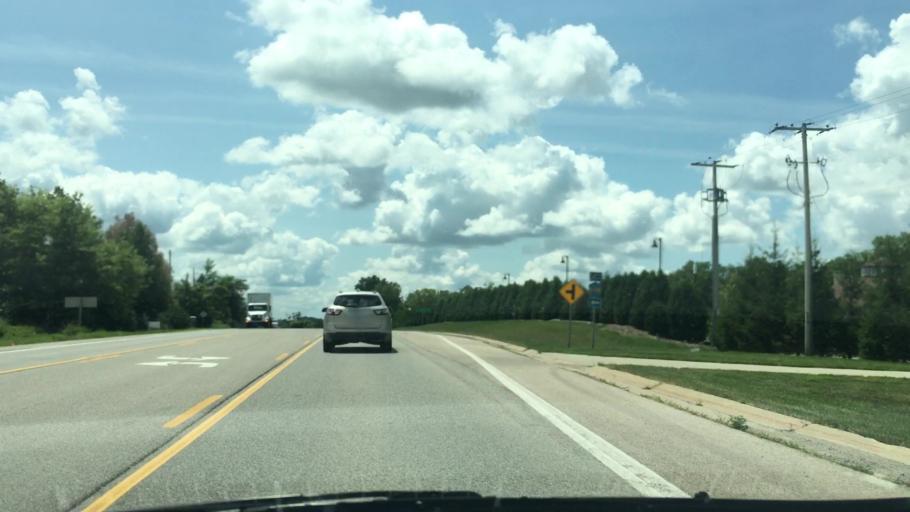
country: US
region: Iowa
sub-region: Johnson County
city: Solon
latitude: 41.7404
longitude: -91.4741
